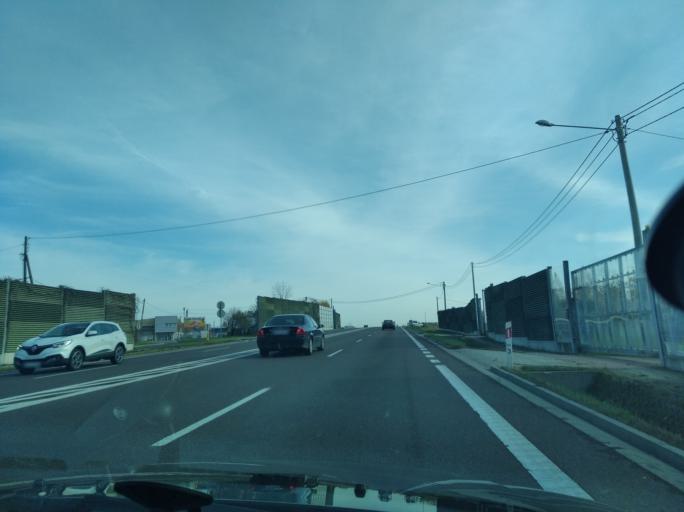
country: PL
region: Subcarpathian Voivodeship
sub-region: Powiat rzeszowski
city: Krasne
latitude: 50.0420
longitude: 22.1044
